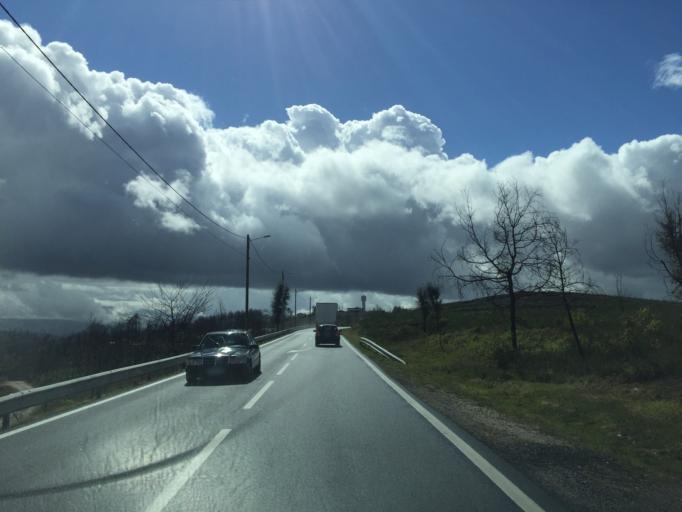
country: PT
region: Coimbra
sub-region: Oliveira do Hospital
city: Oliveira do Hospital
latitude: 40.3378
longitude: -7.8550
